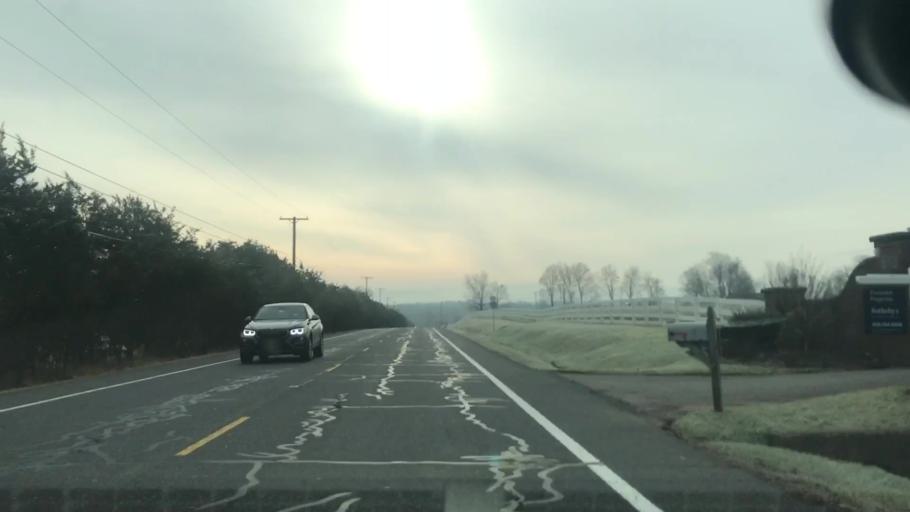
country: US
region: New Jersey
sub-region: Hunterdon County
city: Whitehouse Station
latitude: 40.6308
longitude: -74.7084
